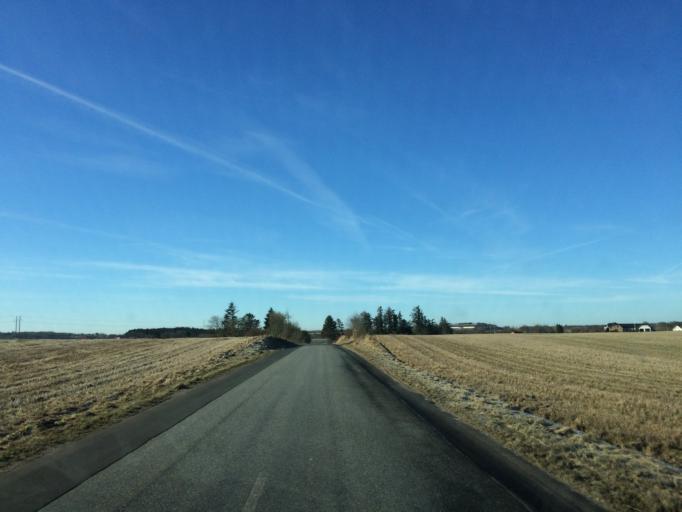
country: DK
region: North Denmark
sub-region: Mariagerfjord Kommune
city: Hobro
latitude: 56.6065
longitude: 9.6331
